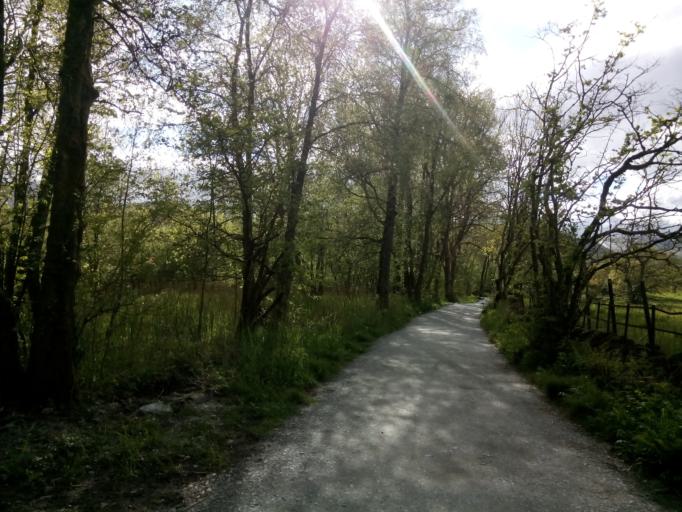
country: GB
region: England
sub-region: Cumbria
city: Ambleside
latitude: 54.4294
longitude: -3.0233
